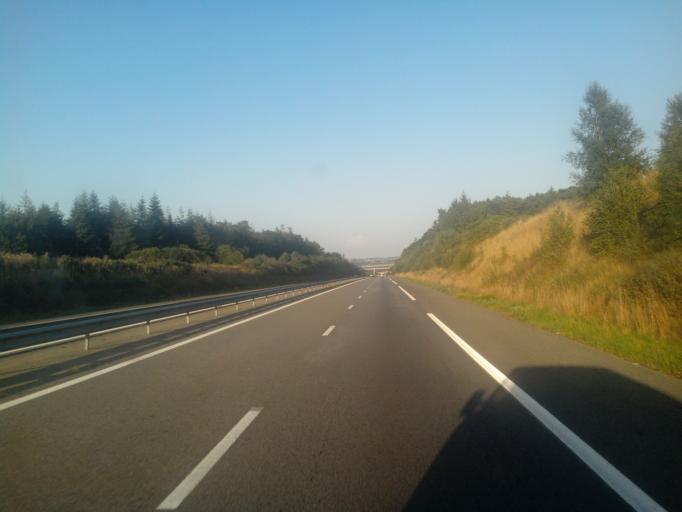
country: FR
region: Brittany
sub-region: Departement du Morbihan
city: Saint-Gonnery
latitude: 48.1296
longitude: -2.8263
